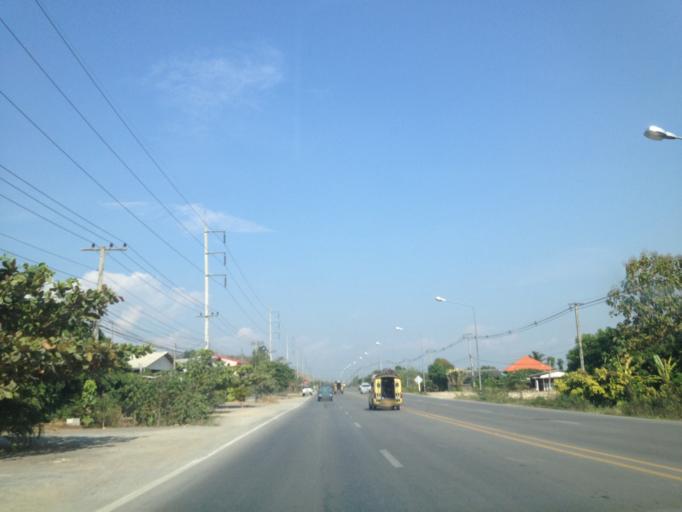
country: TH
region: Chiang Mai
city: Chom Thong
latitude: 18.3537
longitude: 98.6792
